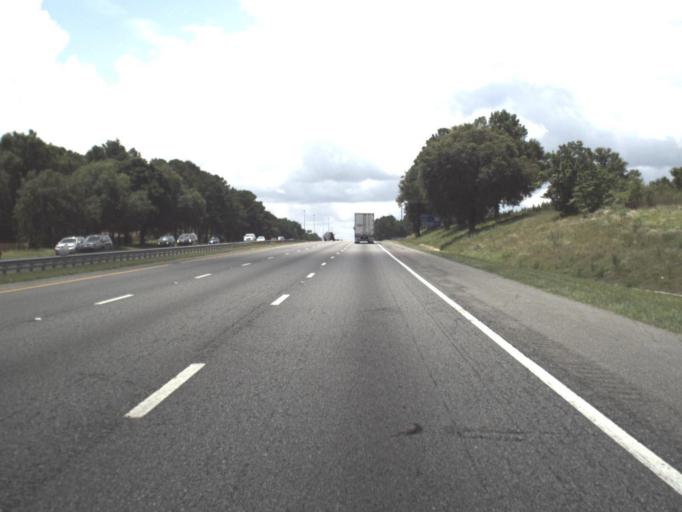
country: US
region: Florida
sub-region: Columbia County
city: Lake City
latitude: 30.1917
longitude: -82.6948
